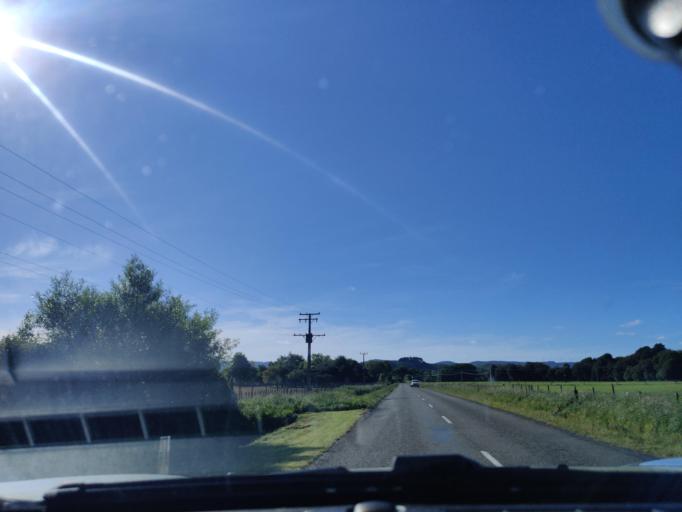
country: NZ
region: Manawatu-Wanganui
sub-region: Palmerston North City
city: Palmerston North
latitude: -40.5243
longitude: 175.7655
